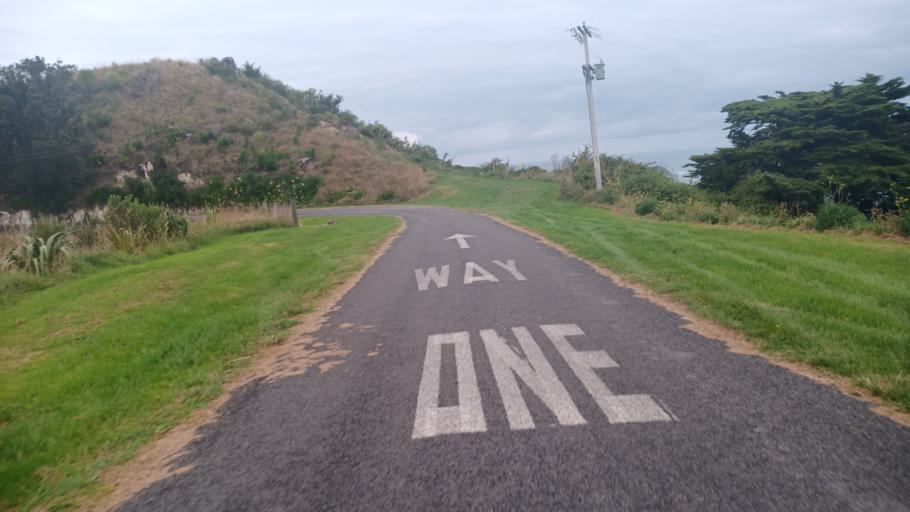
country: NZ
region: Gisborne
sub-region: Gisborne District
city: Gisborne
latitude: -38.6803
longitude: 178.0325
